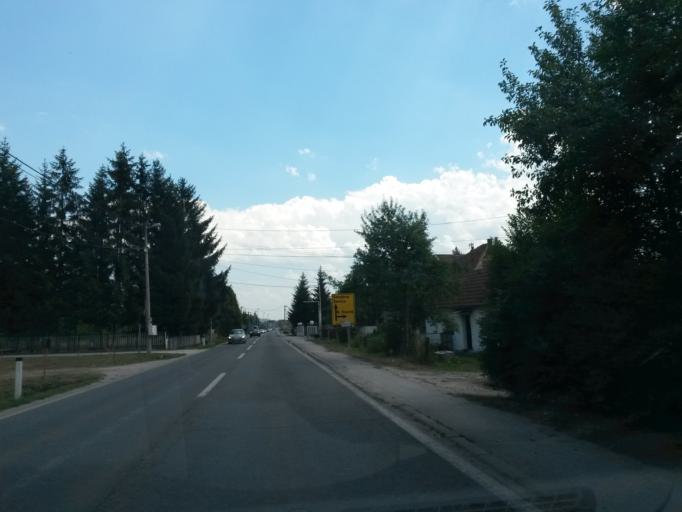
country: BA
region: Federation of Bosnia and Herzegovina
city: Travnik
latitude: 44.2088
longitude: 17.7127
